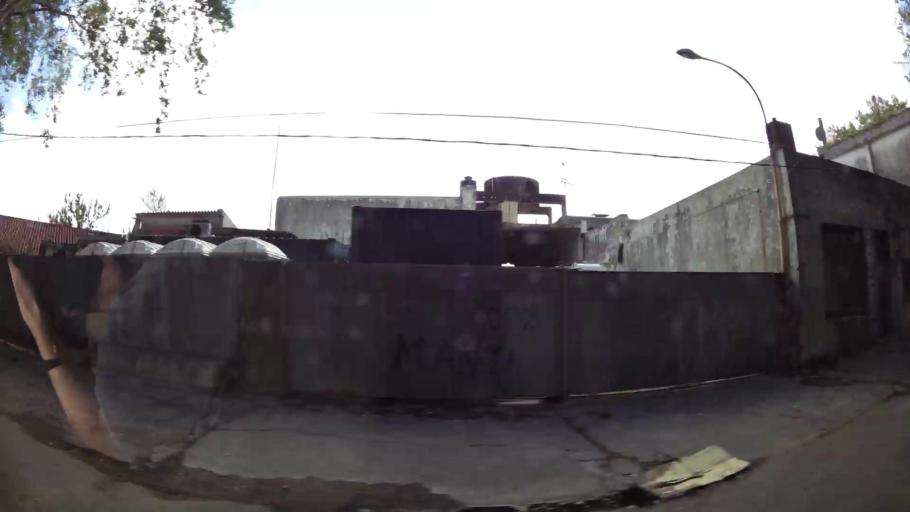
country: UY
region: Canelones
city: La Paz
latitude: -34.8068
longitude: -56.2210
